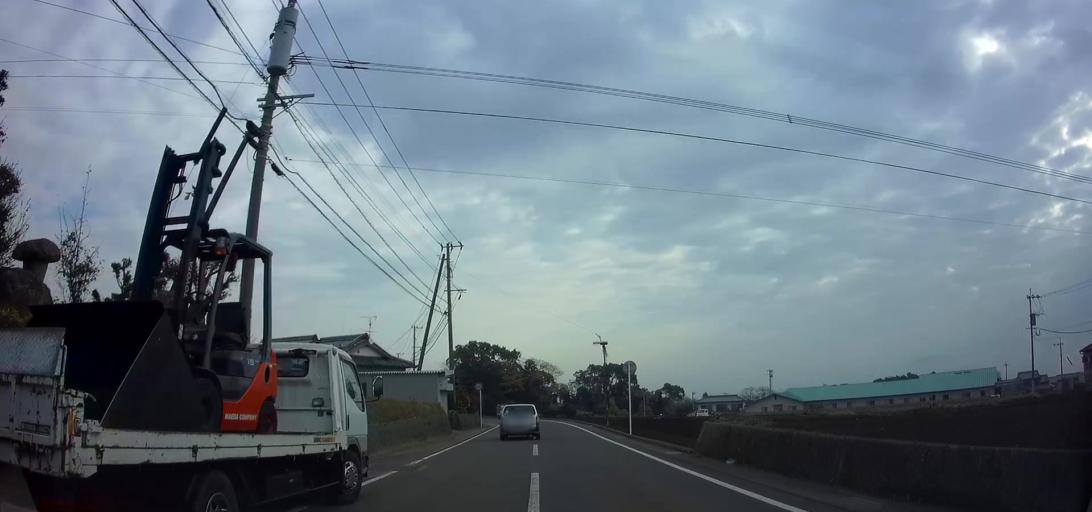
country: JP
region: Nagasaki
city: Shimabara
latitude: 32.6978
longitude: 130.3306
